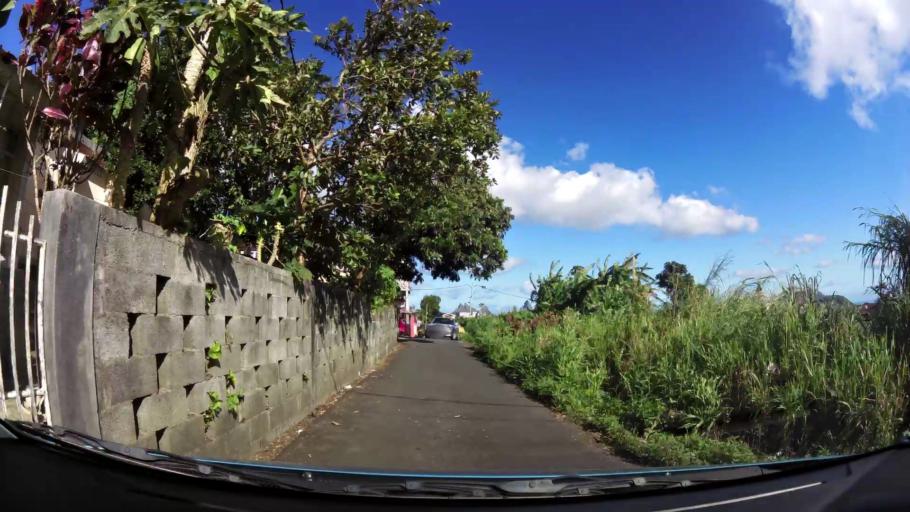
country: MU
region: Plaines Wilhems
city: Curepipe
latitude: -20.2977
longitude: 57.5141
